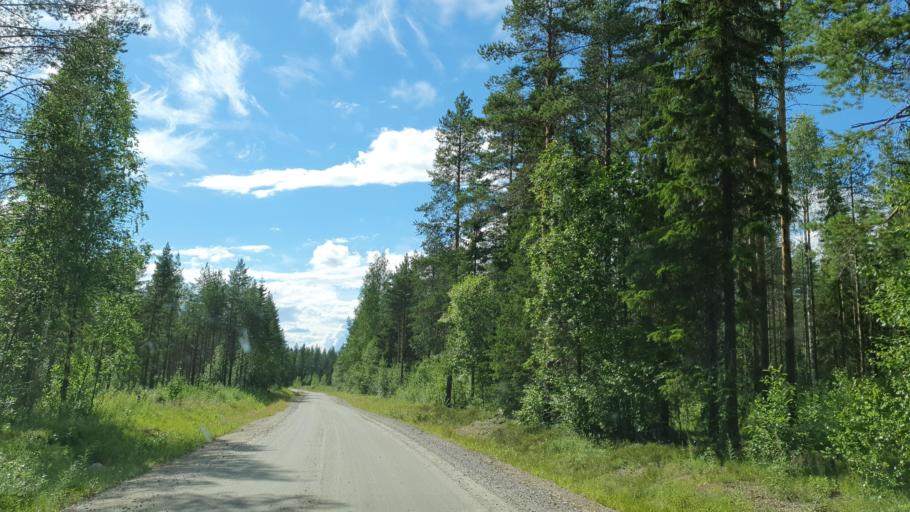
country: FI
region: Kainuu
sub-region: Kehys-Kainuu
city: Kuhmo
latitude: 64.1625
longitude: 29.8434
